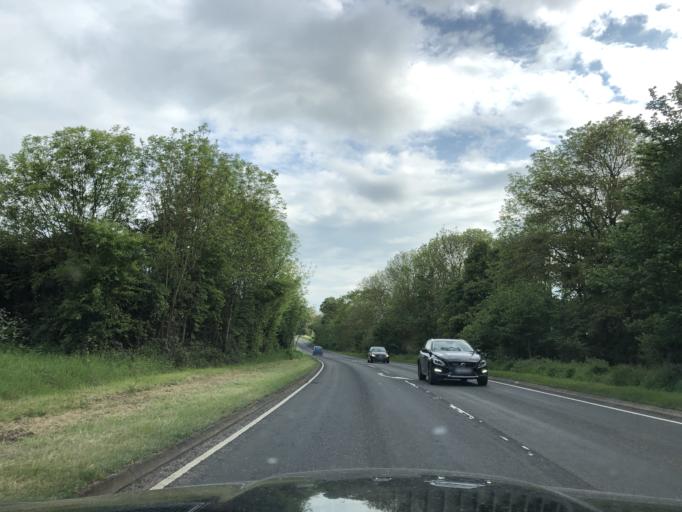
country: GB
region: England
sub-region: Warwickshire
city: Shipston on Stour
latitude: 52.1251
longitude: -1.6191
